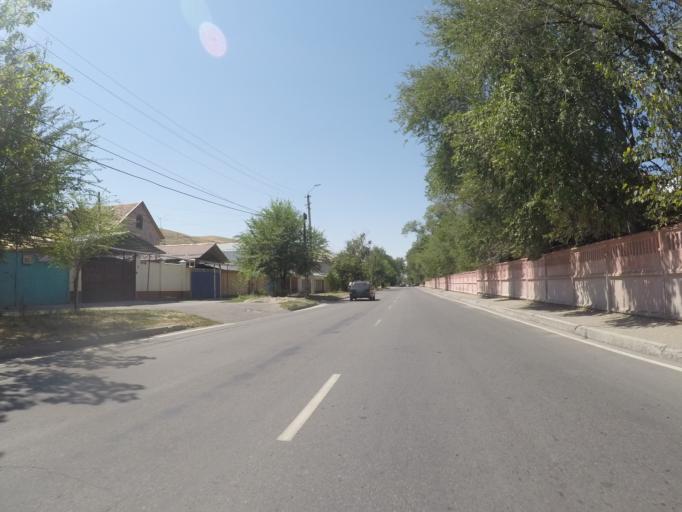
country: KG
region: Chuy
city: Bishkek
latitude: 42.8042
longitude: 74.5759
